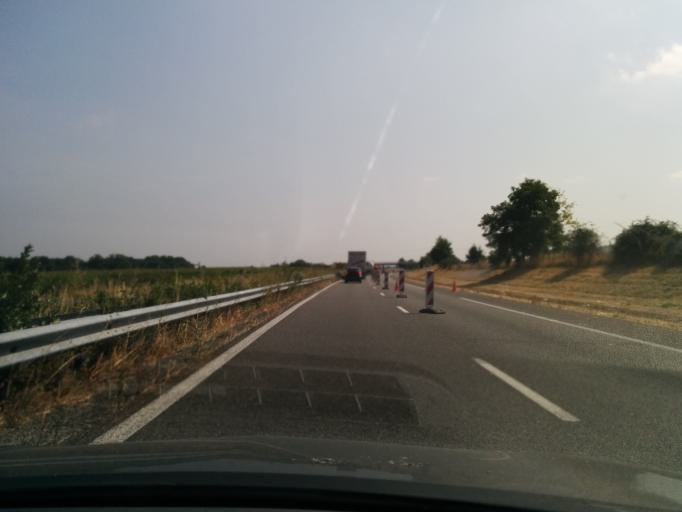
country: FR
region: Midi-Pyrenees
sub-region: Departement de la Haute-Garonne
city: Buzet-sur-Tarn
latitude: 43.7510
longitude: 1.6447
